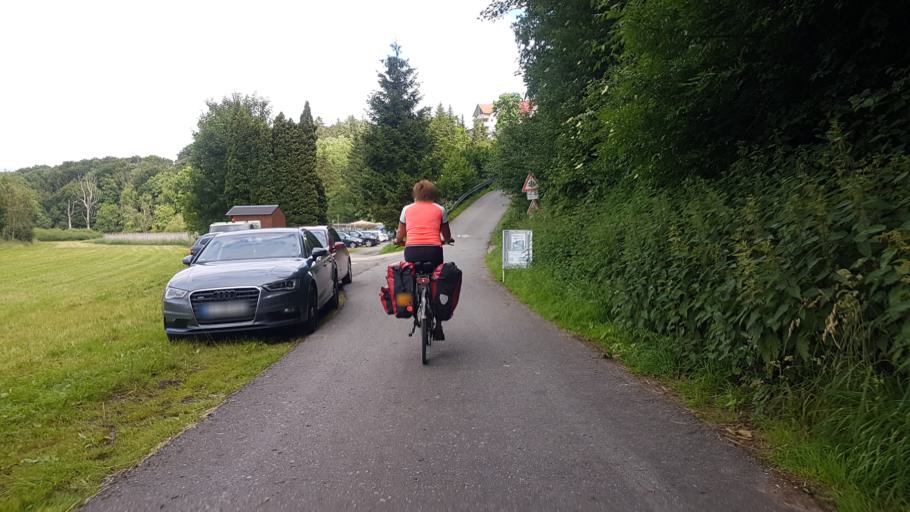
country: DE
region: Baden-Wuerttemberg
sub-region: Tuebingen Region
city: Emeringen
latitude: 48.2166
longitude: 9.5311
